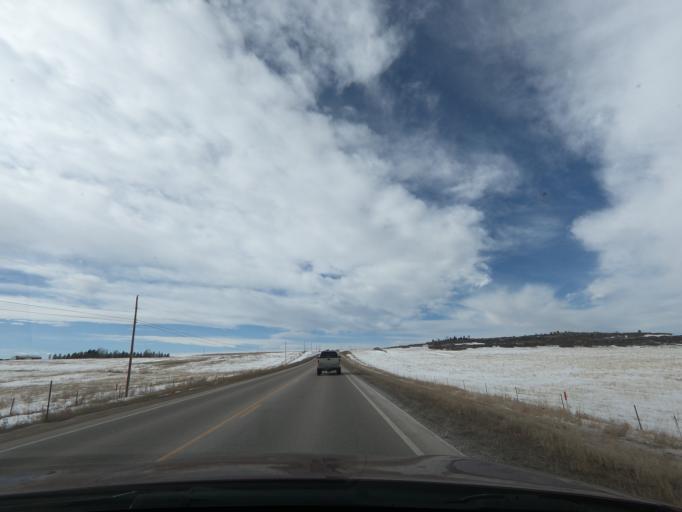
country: US
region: Colorado
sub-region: Elbert County
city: Elizabeth
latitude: 39.2659
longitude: -104.7228
